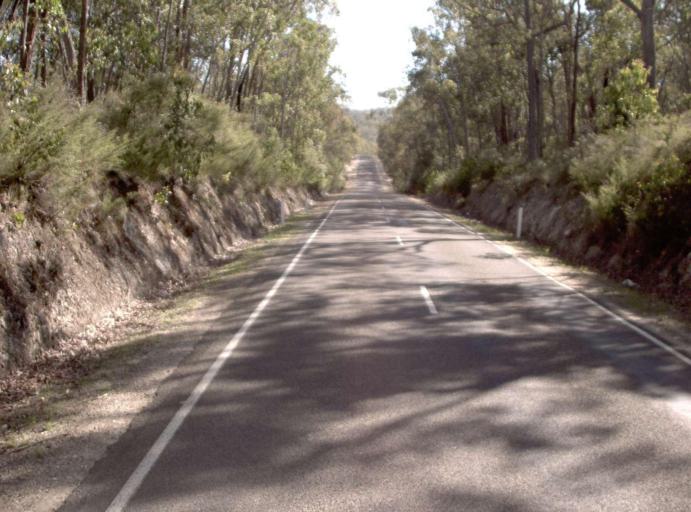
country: AU
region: Victoria
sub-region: East Gippsland
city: Lakes Entrance
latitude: -37.6569
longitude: 148.0907
